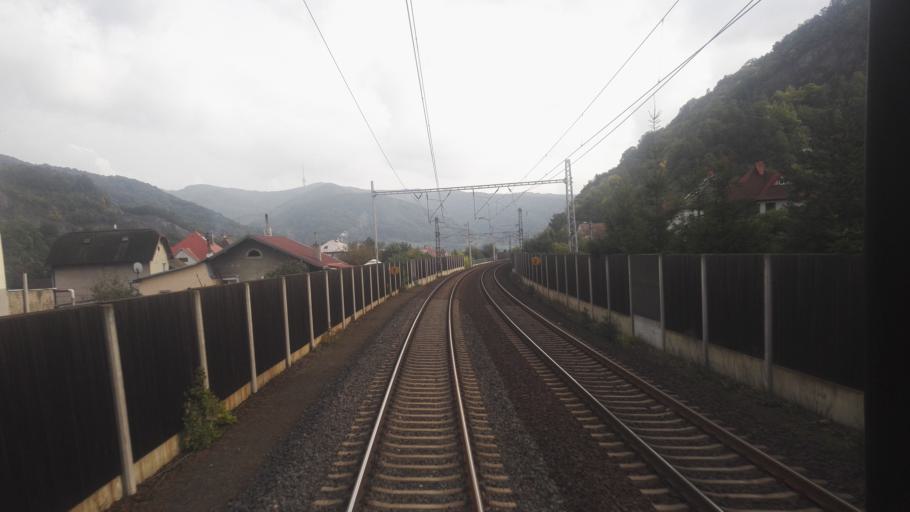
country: CZ
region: Ustecky
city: Povrly
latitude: 50.7137
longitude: 14.1933
